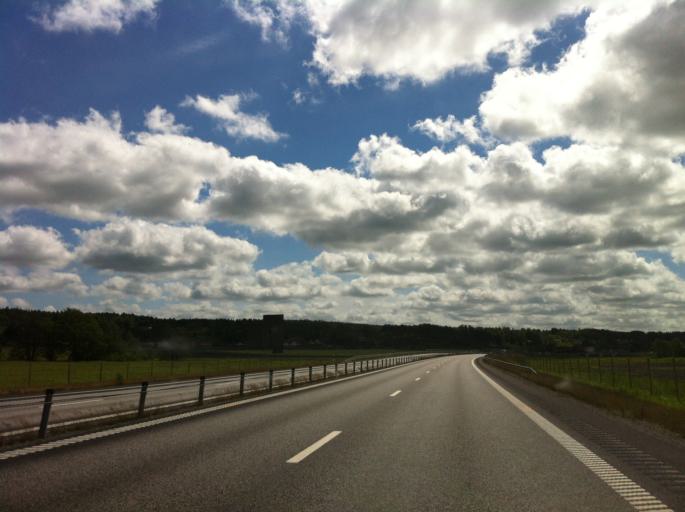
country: SE
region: Vaestra Goetaland
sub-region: Ale Kommun
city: Alvangen
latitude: 57.9770
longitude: 12.1582
